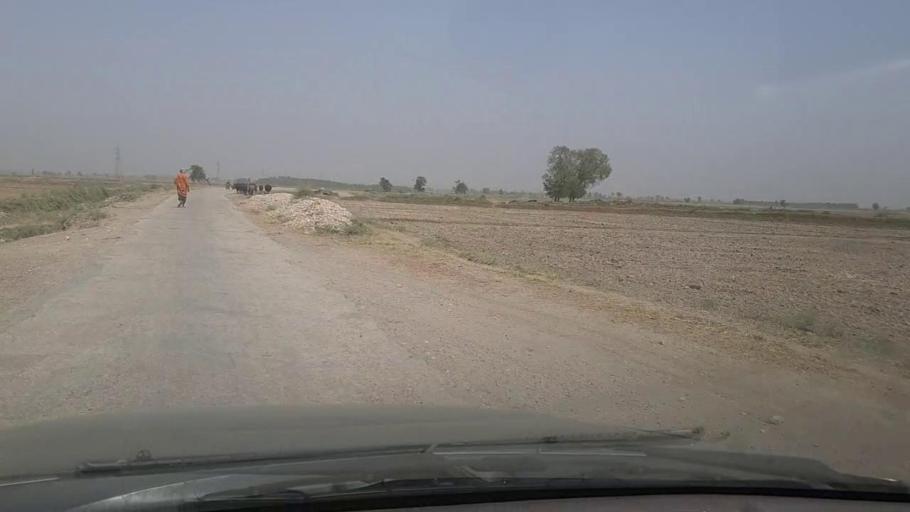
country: PK
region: Sindh
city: Madeji
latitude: 27.8081
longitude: 68.3985
